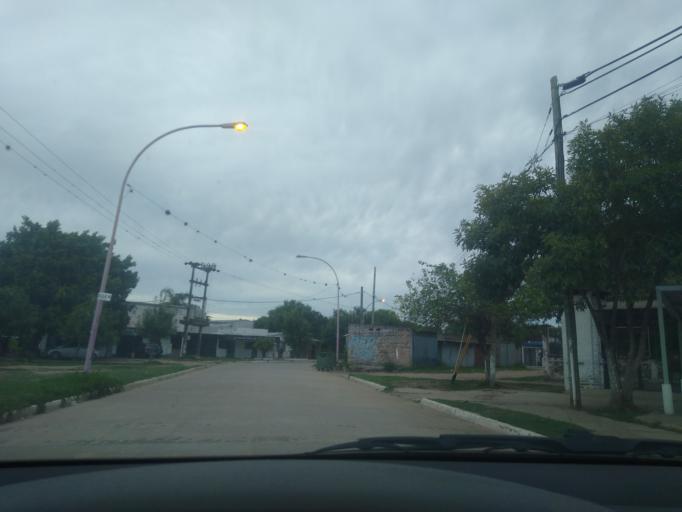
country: AR
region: Chaco
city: Barranqueras
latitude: -27.4649
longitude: -58.9478
